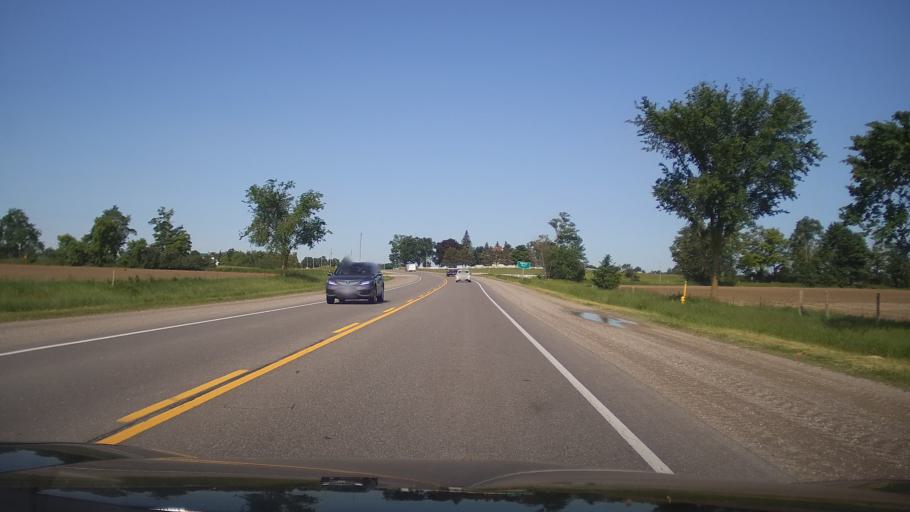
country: CA
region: Ontario
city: Omemee
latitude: 44.3464
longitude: -78.8184
